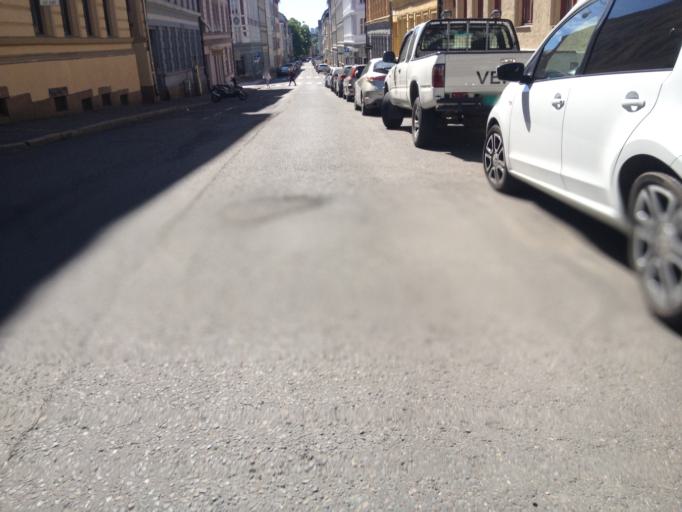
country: NO
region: Oslo
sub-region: Oslo
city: Oslo
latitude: 59.9263
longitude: 10.7571
